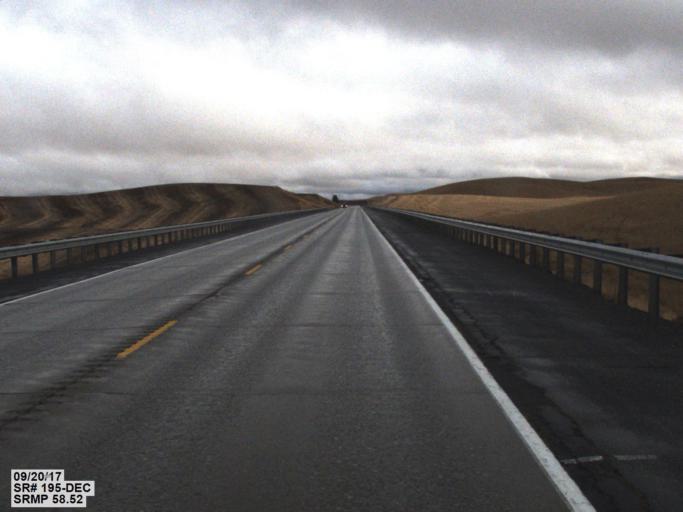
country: US
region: Washington
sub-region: Whitman County
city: Colfax
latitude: 47.1534
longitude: -117.3789
